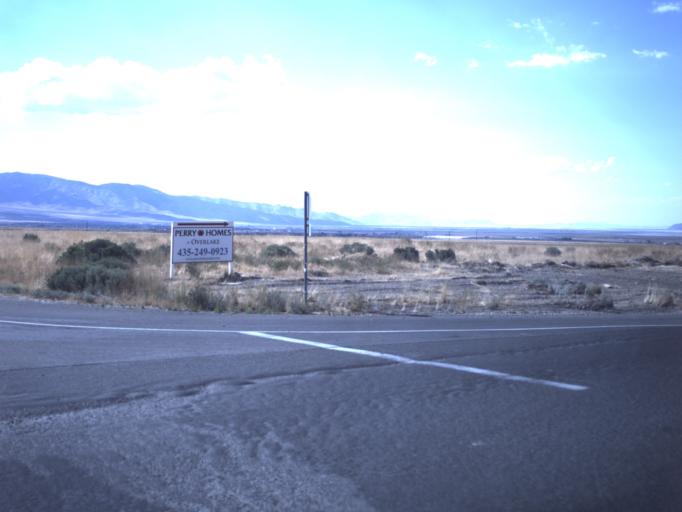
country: US
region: Utah
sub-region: Tooele County
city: Tooele
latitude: 40.5509
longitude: -112.3171
